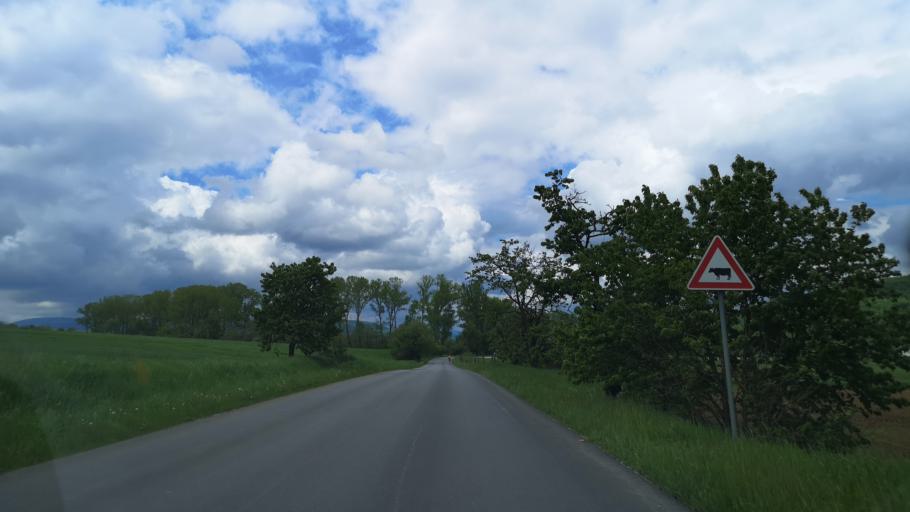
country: SK
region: Kosicky
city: Dobsina
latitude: 48.6666
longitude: 20.3591
